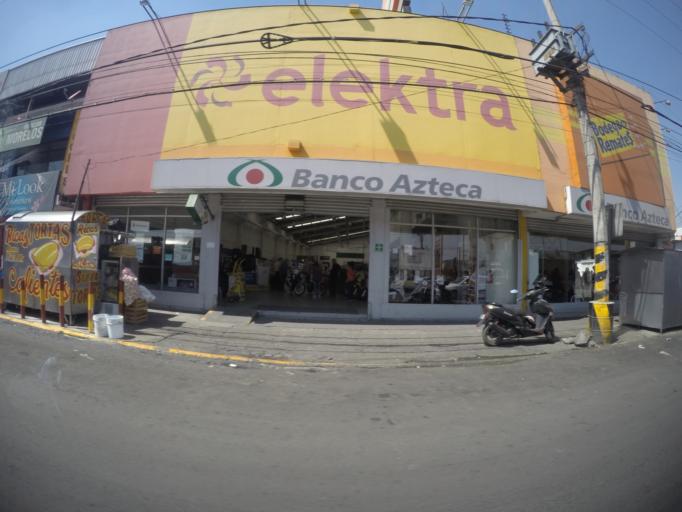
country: MX
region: Mexico
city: Ecatepec
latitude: 19.5952
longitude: -99.0379
